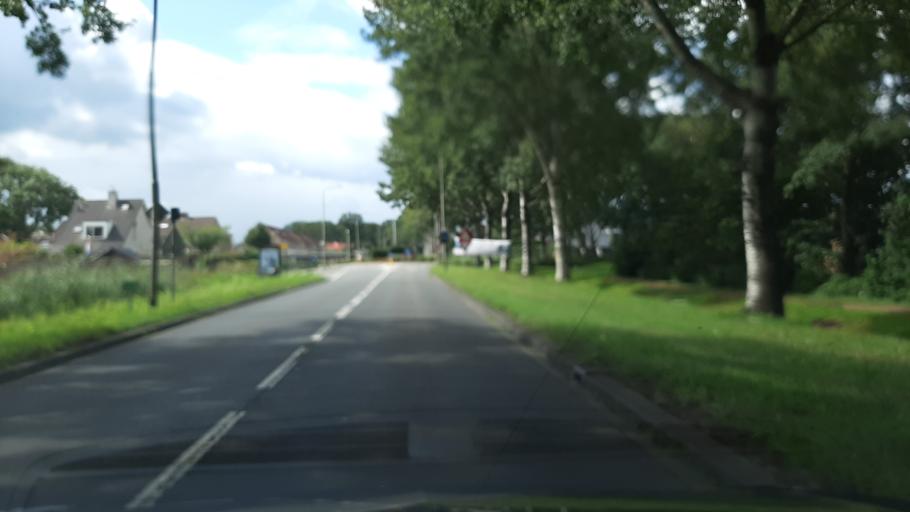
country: NL
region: Overijssel
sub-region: Gemeente Zwartewaterland
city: Hasselt
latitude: 52.6442
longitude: 6.0793
